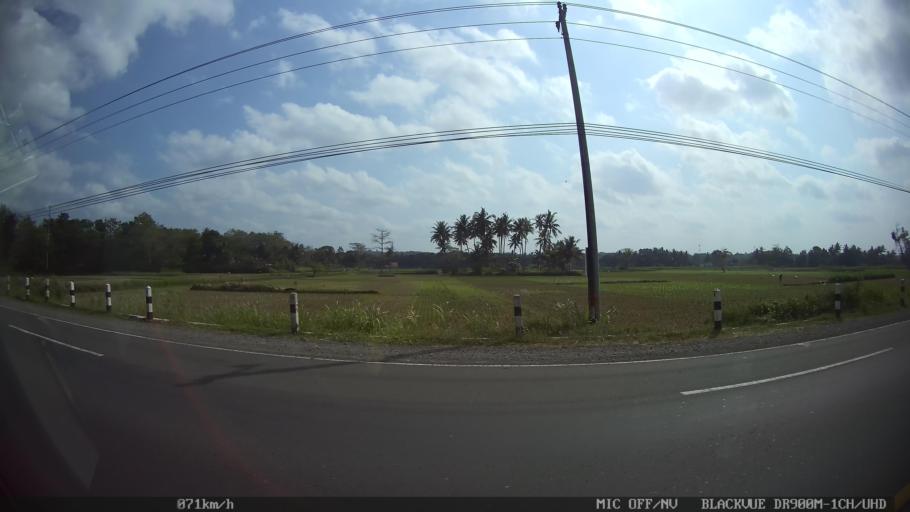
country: ID
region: Daerah Istimewa Yogyakarta
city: Srandakan
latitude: -7.8731
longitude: 110.2000
